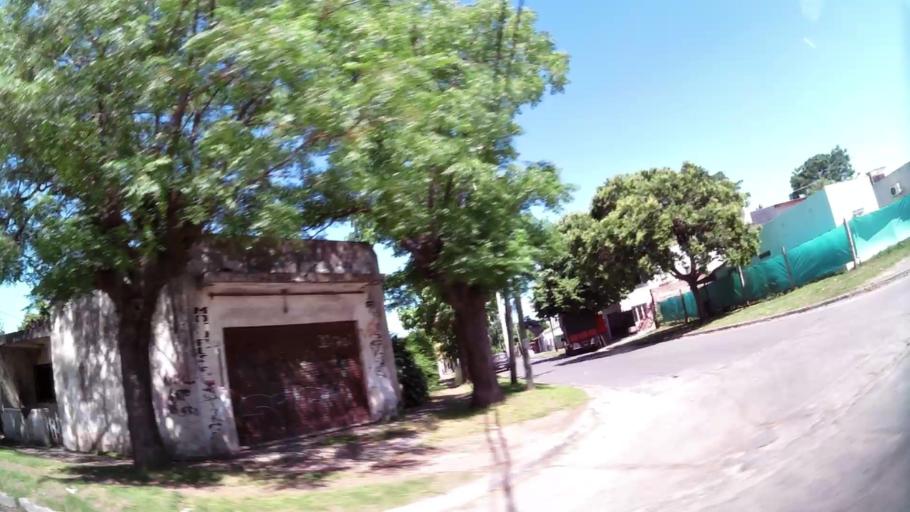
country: AR
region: Buenos Aires
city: Hurlingham
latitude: -34.5102
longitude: -58.6748
